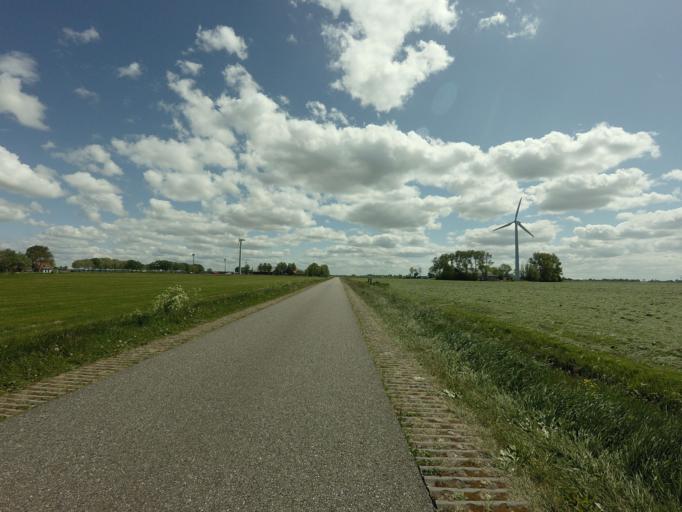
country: NL
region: Friesland
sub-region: Sudwest Fryslan
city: Makkum
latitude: 53.0926
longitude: 5.4086
